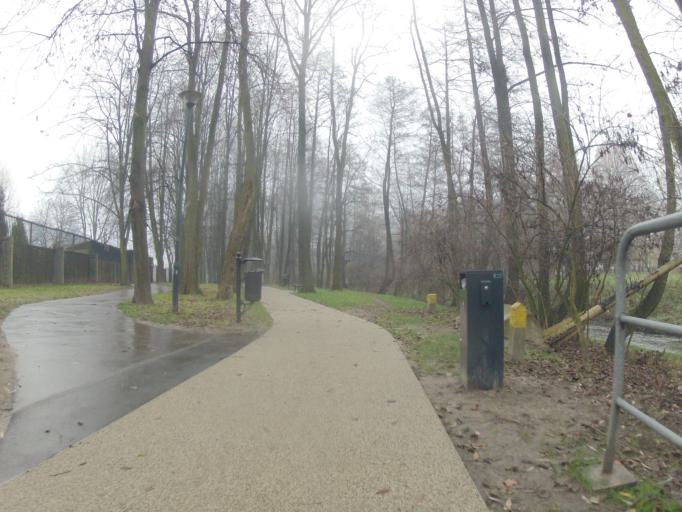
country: PL
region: Lesser Poland Voivodeship
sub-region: Powiat krakowski
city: Zielonki
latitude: 50.0947
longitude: 19.9403
